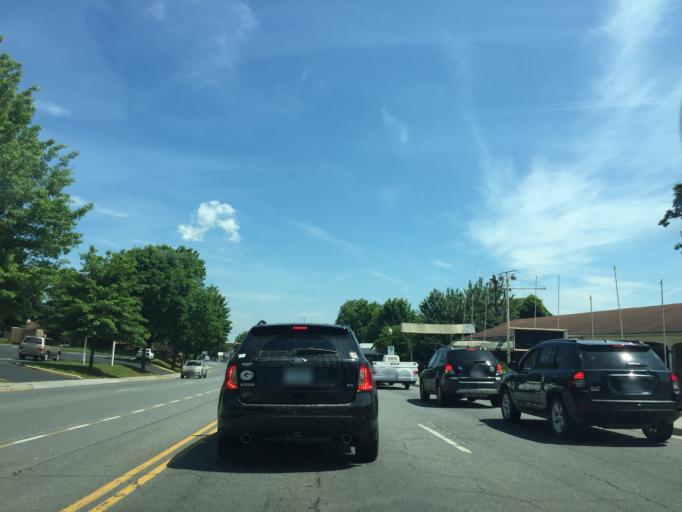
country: US
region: Virginia
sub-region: Warren County
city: Front Royal
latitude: 38.9106
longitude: -78.1951
